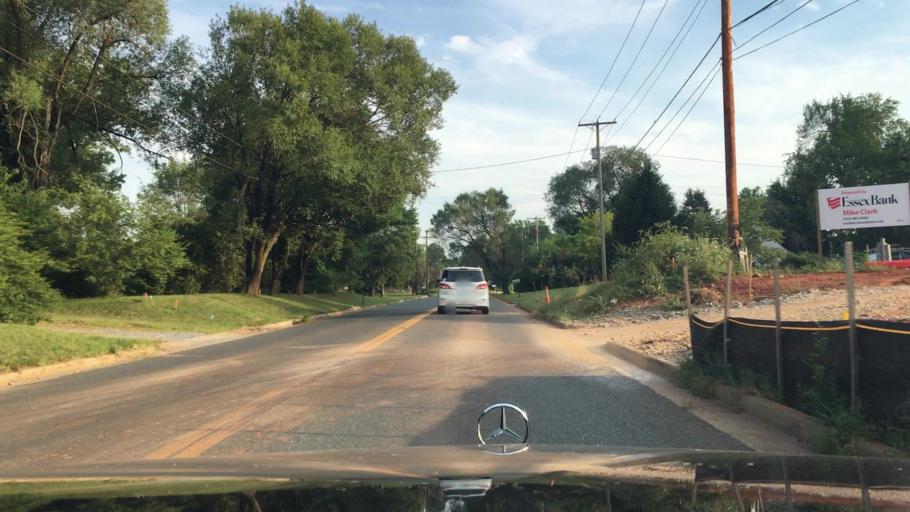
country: US
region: Virginia
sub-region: City of Lynchburg
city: West Lynchburg
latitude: 37.3719
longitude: -79.2262
